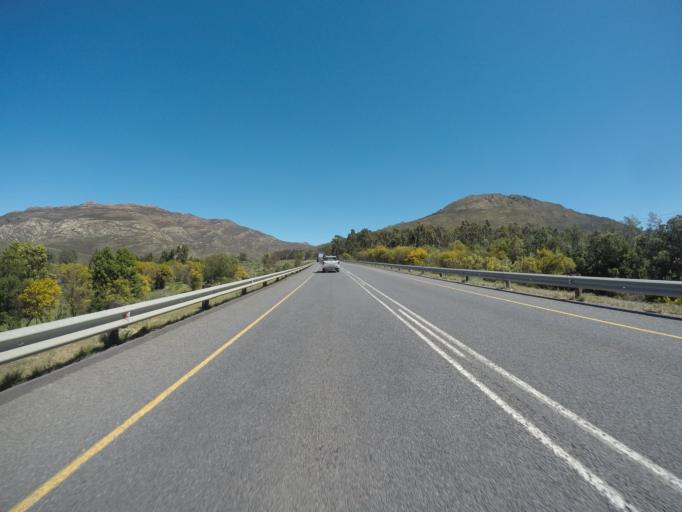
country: ZA
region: Western Cape
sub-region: Cape Winelands District Municipality
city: Ceres
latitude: -33.3111
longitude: 19.0989
